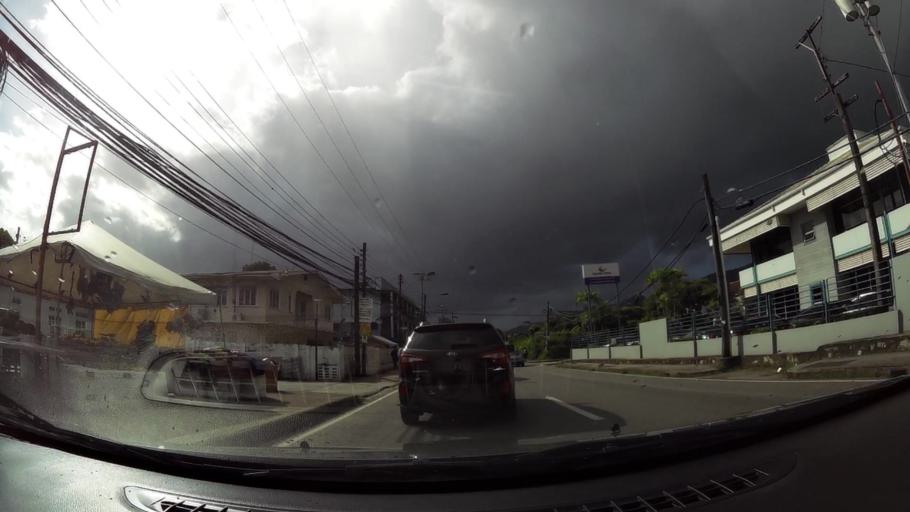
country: TT
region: Tunapuna/Piarco
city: Tunapuna
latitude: 10.6460
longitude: -61.3987
